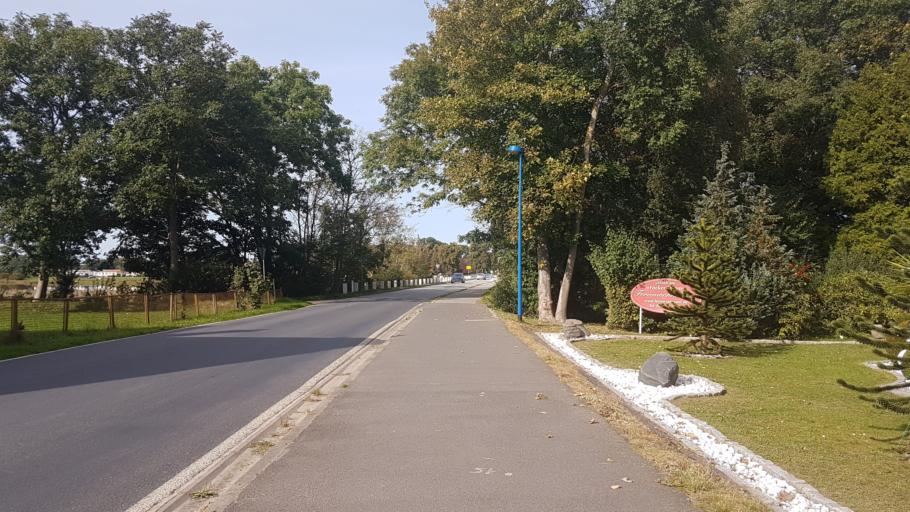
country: DE
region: Mecklenburg-Vorpommern
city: Gingst
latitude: 54.4538
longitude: 13.1808
